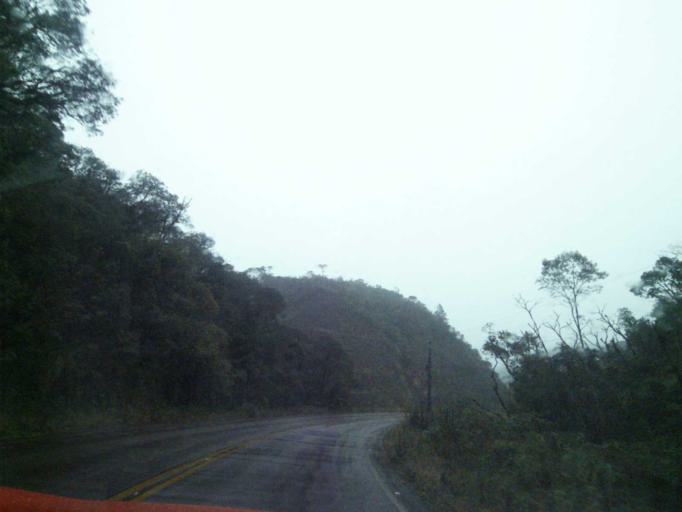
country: BR
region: Santa Catarina
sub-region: Anitapolis
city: Anitapolis
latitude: -27.7481
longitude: -49.0345
